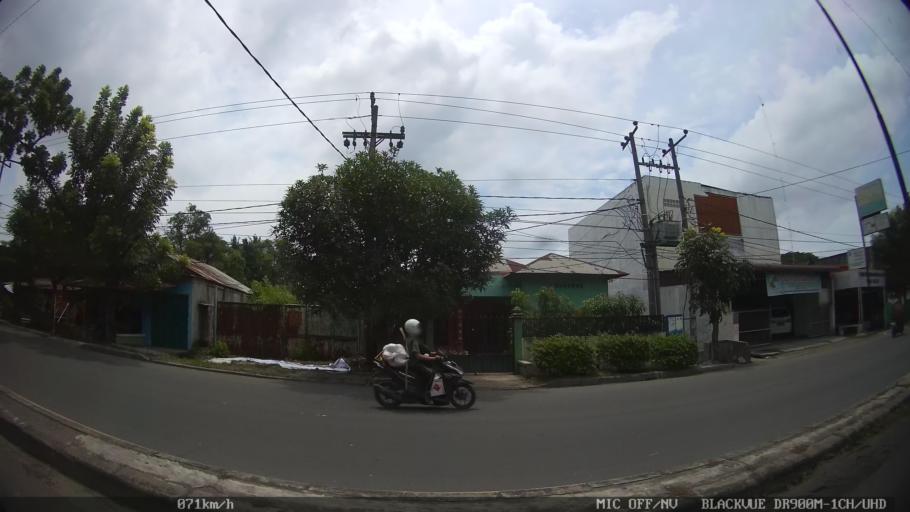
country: ID
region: North Sumatra
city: Labuhan Deli
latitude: 3.6643
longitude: 98.6666
